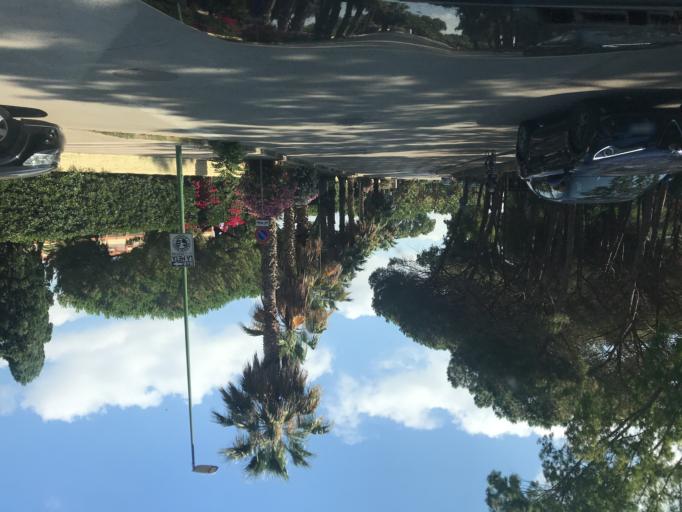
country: IT
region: Sardinia
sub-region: Provincia di Sassari
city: Alghero
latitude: 40.5834
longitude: 8.3110
